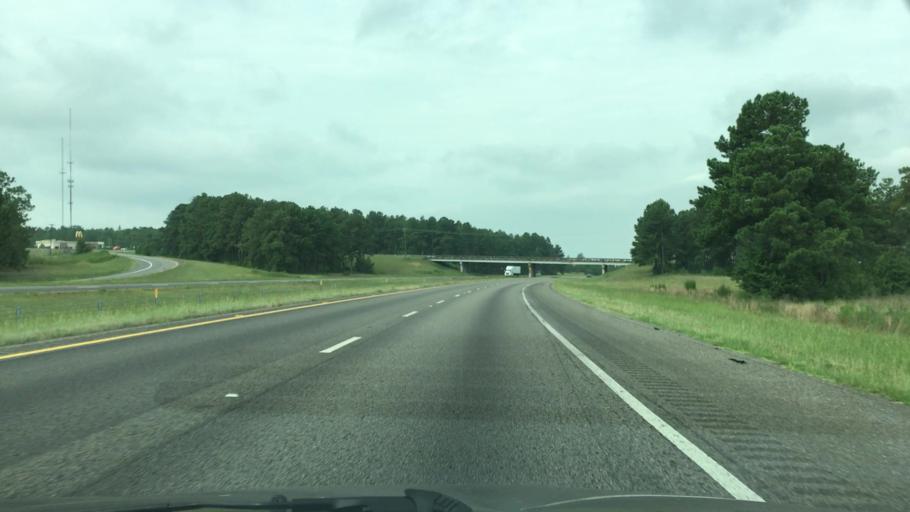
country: US
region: South Carolina
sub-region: Aiken County
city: Graniteville
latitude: 33.6082
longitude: -81.8409
